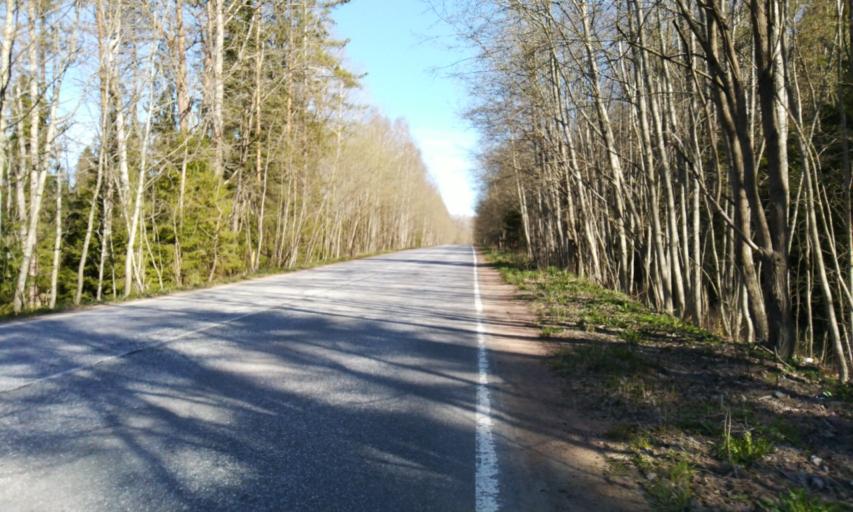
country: RU
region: Leningrad
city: Garbolovo
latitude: 60.3647
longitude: 30.4422
